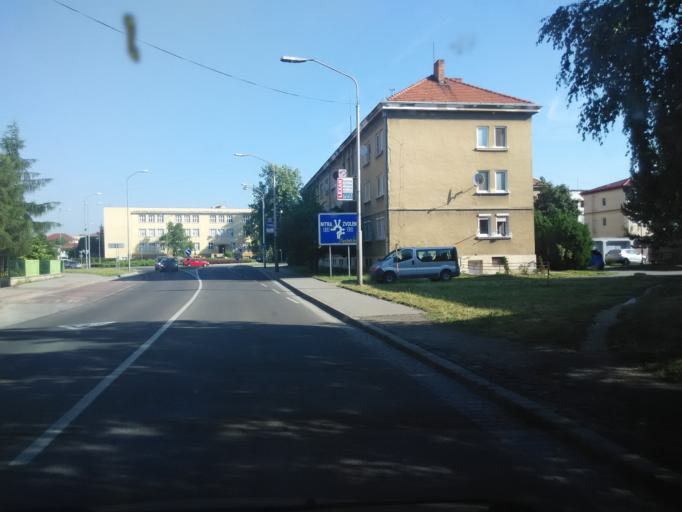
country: SK
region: Nitriansky
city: Levice
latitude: 48.2143
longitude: 18.5948
